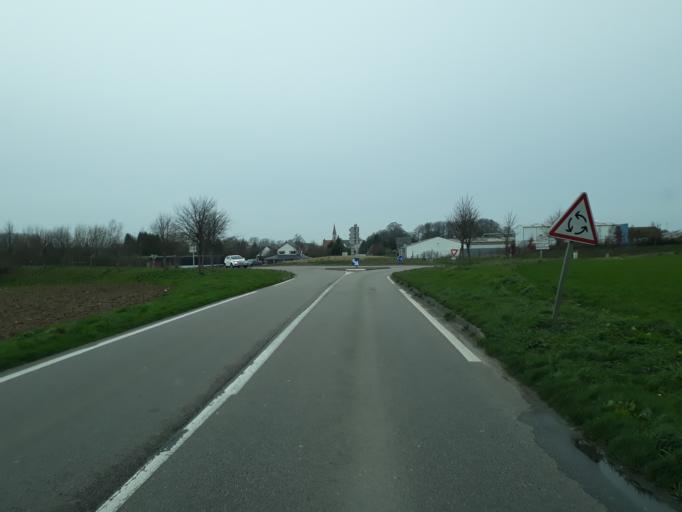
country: FR
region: Haute-Normandie
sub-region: Departement de la Seine-Maritime
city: Goderville
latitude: 49.6407
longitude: 0.3773
